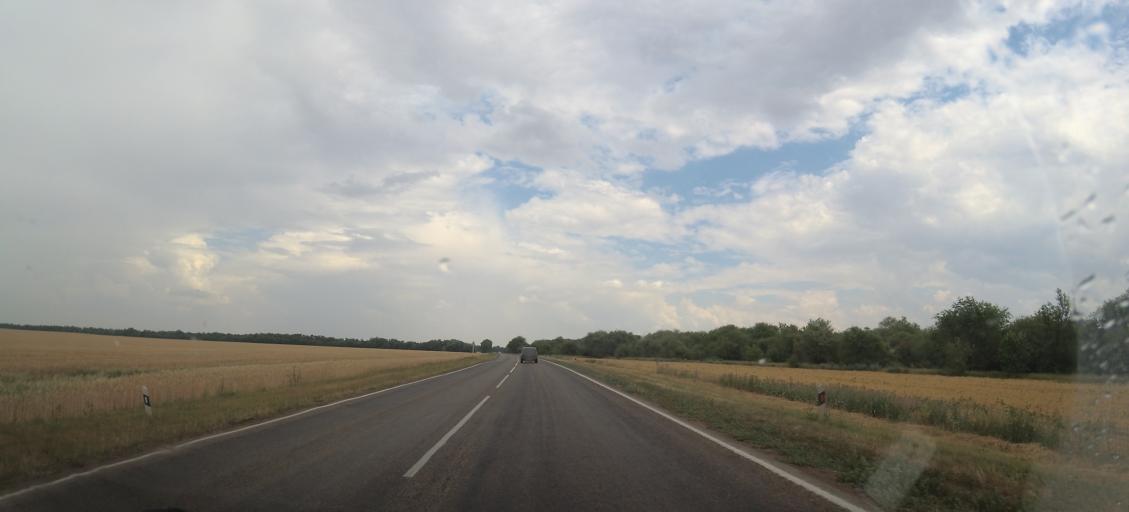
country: RU
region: Rostov
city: Peschanokopskoye
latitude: 46.2004
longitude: 41.1830
